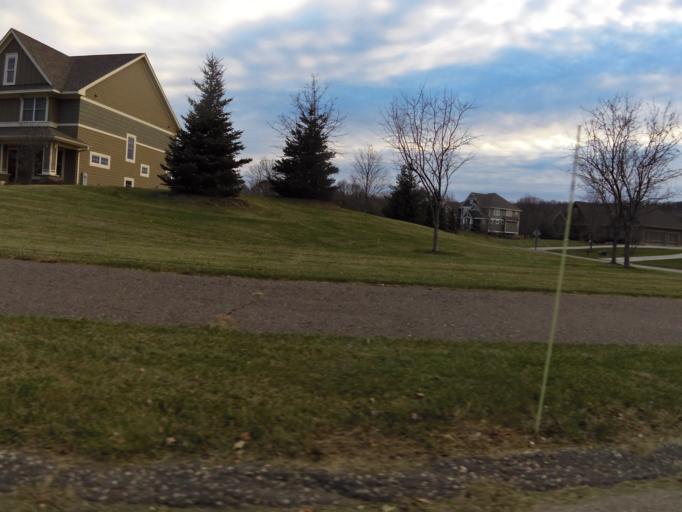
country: US
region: Minnesota
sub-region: Washington County
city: Bayport
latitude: 44.9993
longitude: -92.7966
